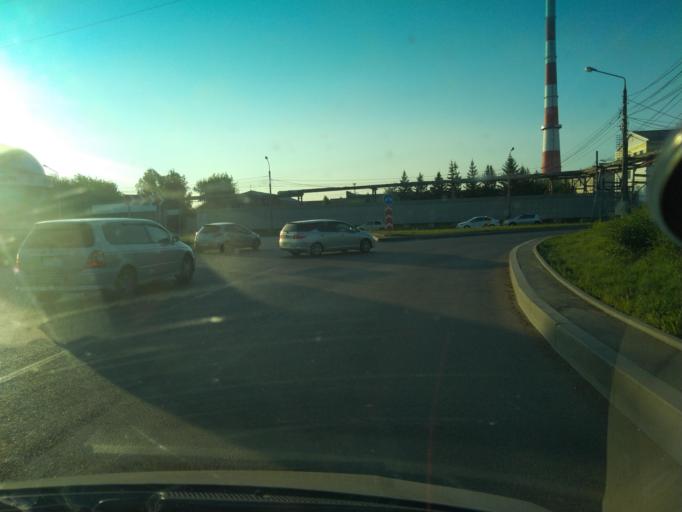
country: RU
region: Krasnoyarskiy
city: Berezovka
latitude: 56.0186
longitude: 93.0312
